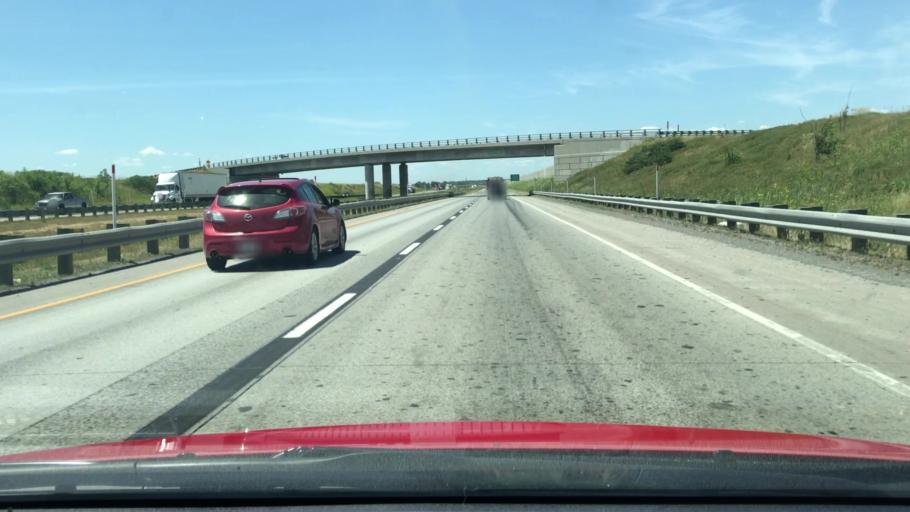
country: CA
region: Quebec
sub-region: Monteregie
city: Saint-Constant
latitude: 45.3593
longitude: -73.5753
